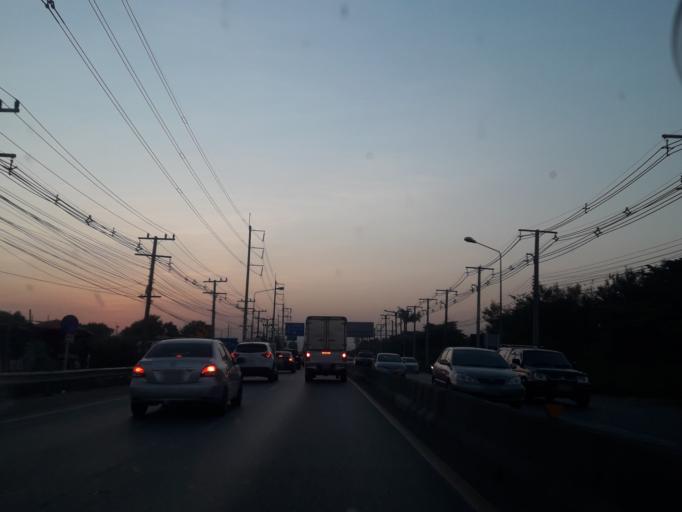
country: TH
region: Pathum Thani
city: Khlong Luang
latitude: 14.0671
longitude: 100.7016
